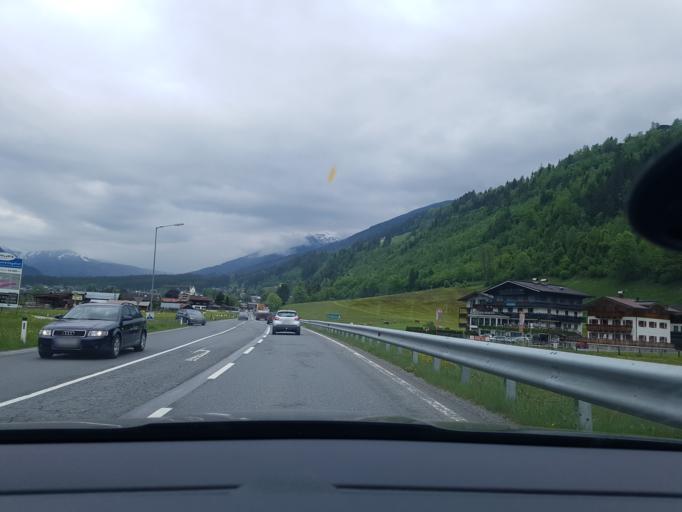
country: AT
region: Salzburg
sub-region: Politischer Bezirk Zell am See
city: Neukirchen am Grossvenediger
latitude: 47.2546
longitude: 12.2901
